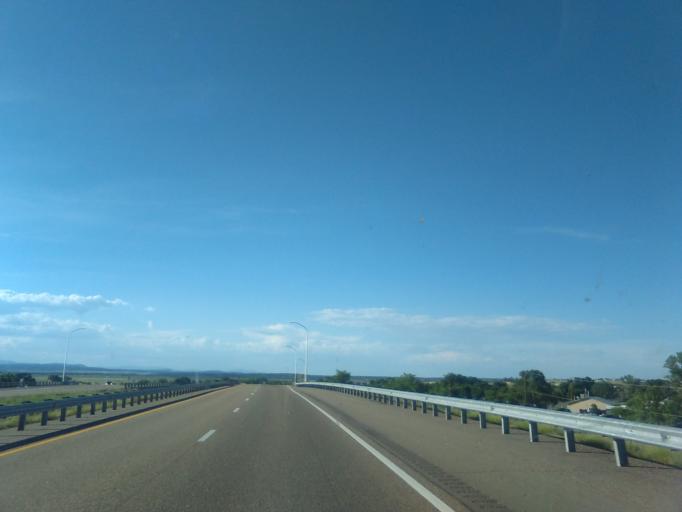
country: US
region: New Mexico
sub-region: San Miguel County
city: Las Vegas
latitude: 35.6197
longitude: -105.2029
